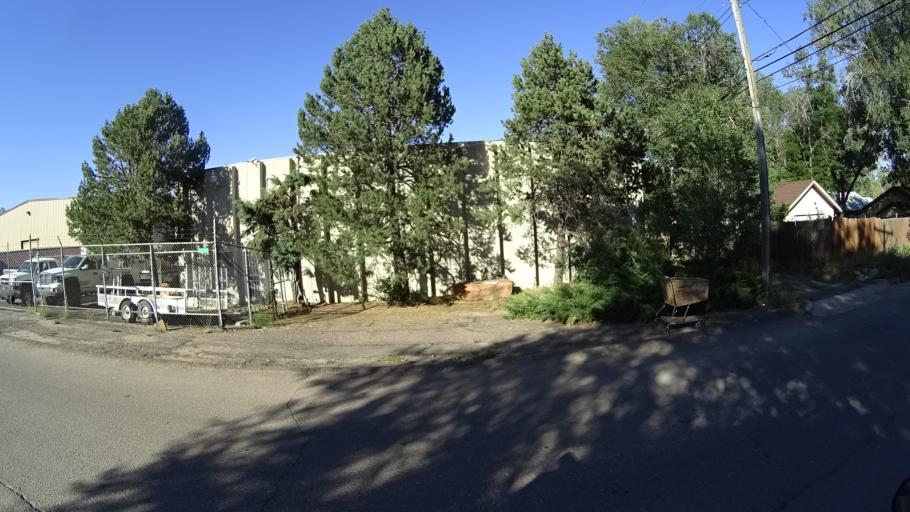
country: US
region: Colorado
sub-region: El Paso County
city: Colorado Springs
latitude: 38.8448
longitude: -104.8685
